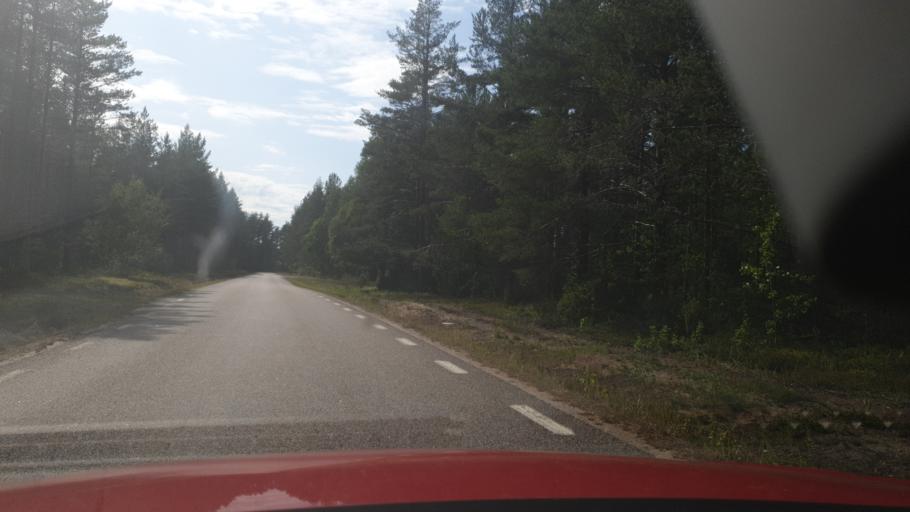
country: SE
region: Vaesternorrland
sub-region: Sundsvalls Kommun
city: Njurundabommen
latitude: 62.0374
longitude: 17.3839
